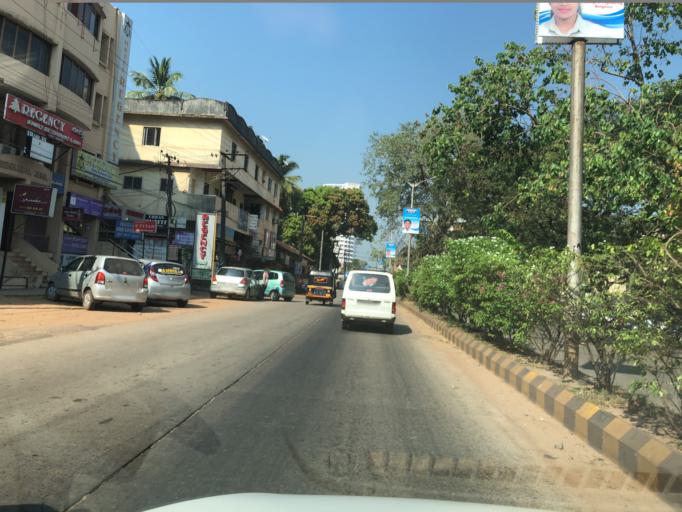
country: IN
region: Karnataka
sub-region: Dakshina Kannada
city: Mangalore
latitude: 12.9043
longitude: 74.8355
